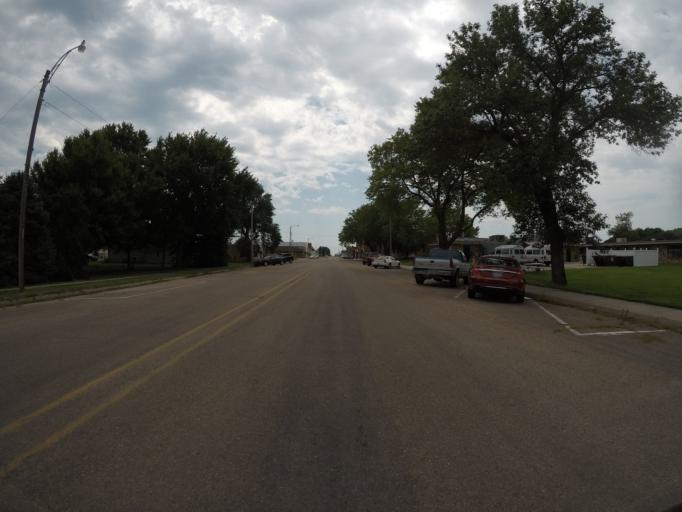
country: US
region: Nebraska
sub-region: Buffalo County
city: Shelton
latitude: 40.6230
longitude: -98.6577
